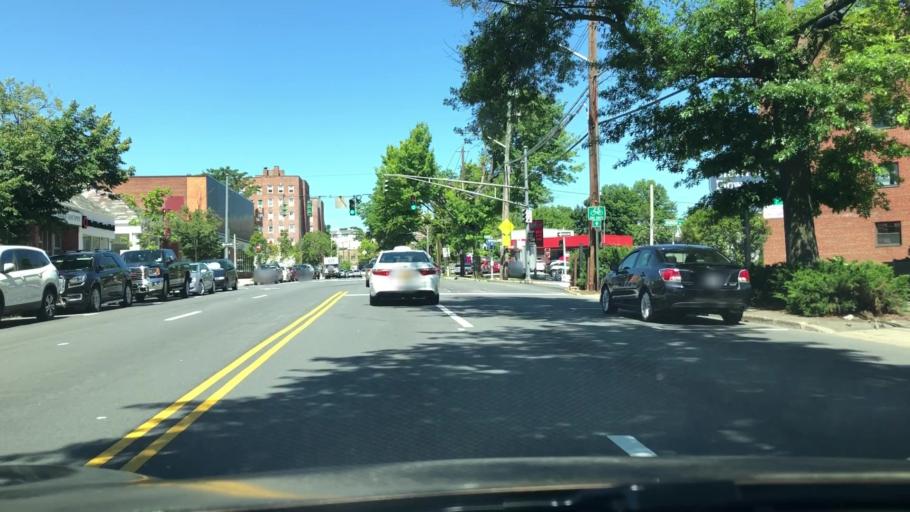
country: US
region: New York
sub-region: Westchester County
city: White Plains
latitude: 41.0227
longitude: -73.7596
